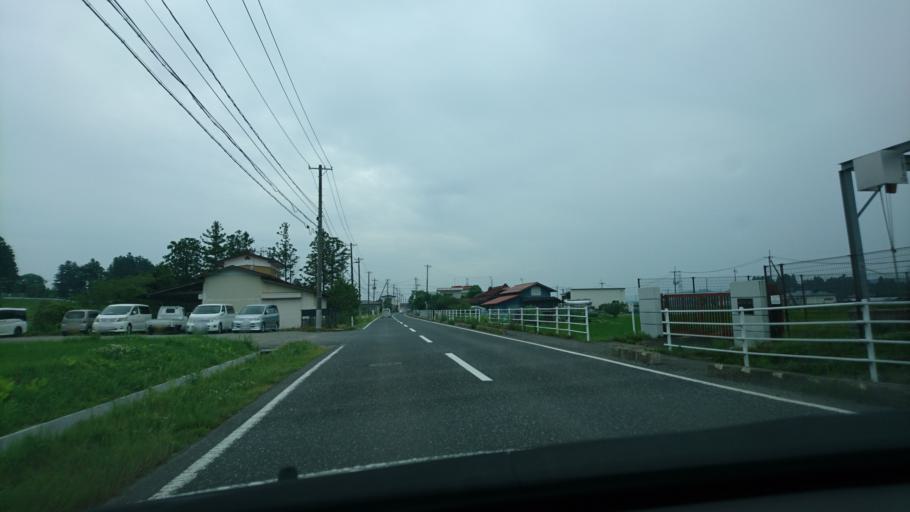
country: JP
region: Miyagi
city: Furukawa
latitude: 38.7300
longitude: 140.9835
